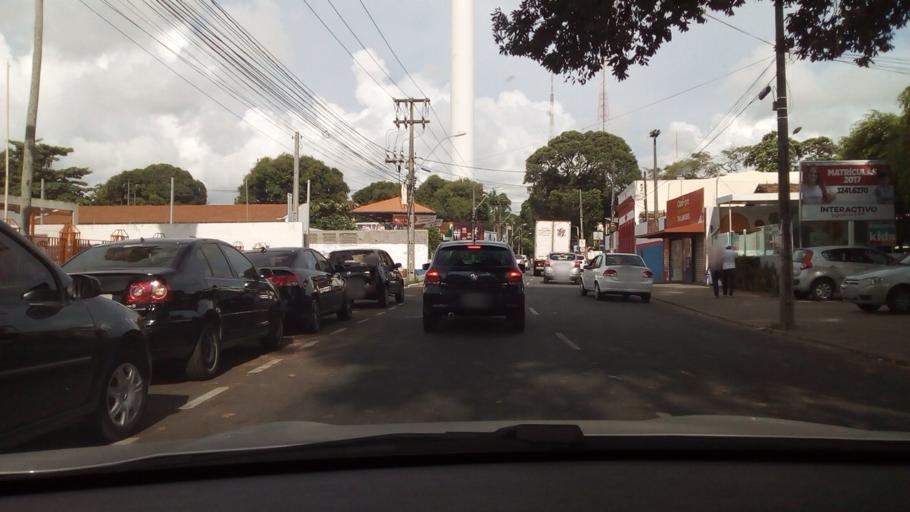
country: BR
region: Paraiba
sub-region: Joao Pessoa
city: Joao Pessoa
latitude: -7.1171
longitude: -34.8739
